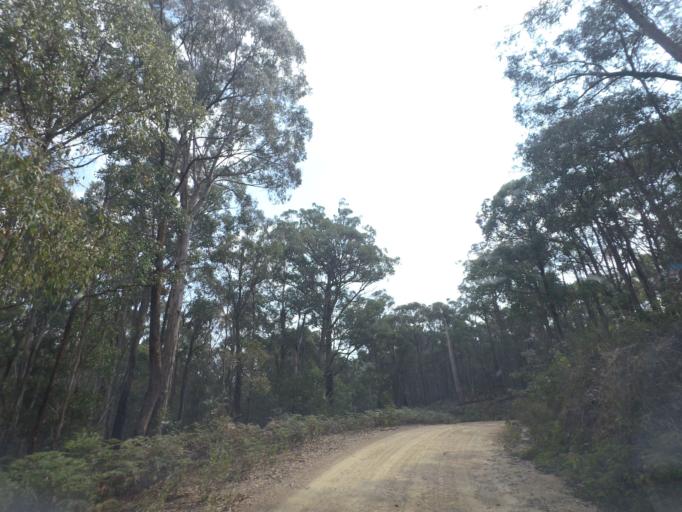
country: AU
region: Victoria
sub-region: Moorabool
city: Bacchus Marsh
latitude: -37.4609
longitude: 144.3839
